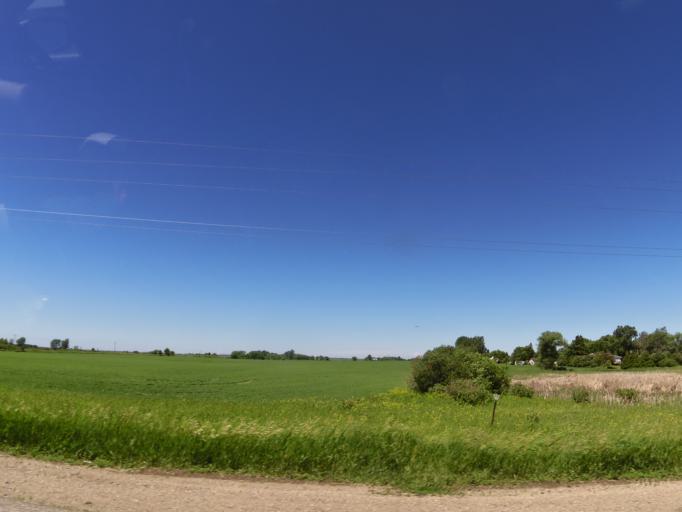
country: US
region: Minnesota
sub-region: Mahnomen County
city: Mahnomen
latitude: 47.1787
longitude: -95.9332
